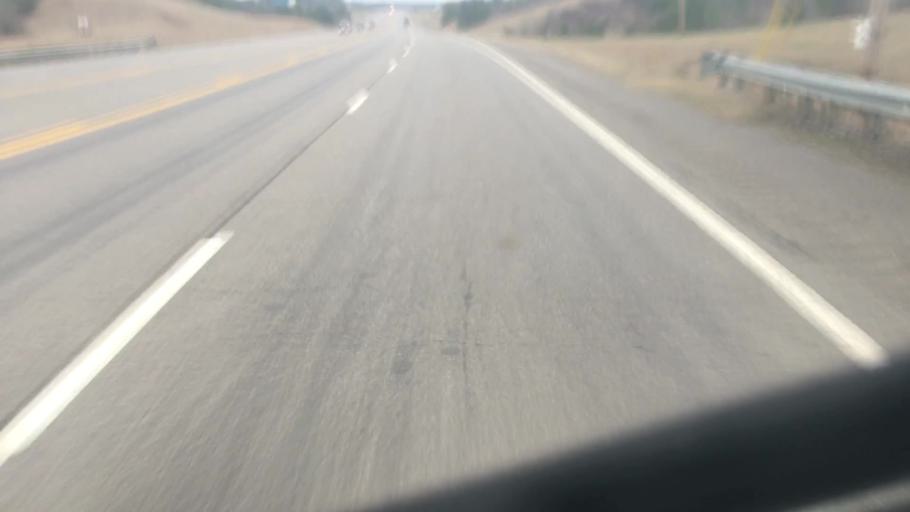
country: US
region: Alabama
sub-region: Walker County
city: Jasper
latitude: 33.8024
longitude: -87.2357
